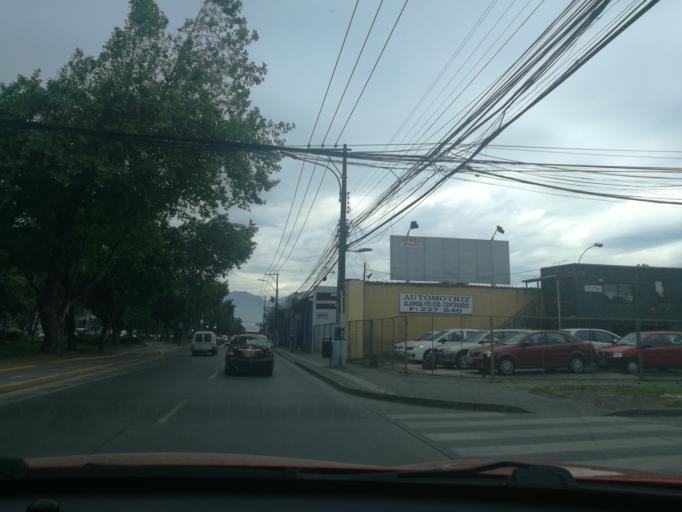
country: CL
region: O'Higgins
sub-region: Provincia de Cachapoal
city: Rancagua
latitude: -34.1662
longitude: -70.7329
